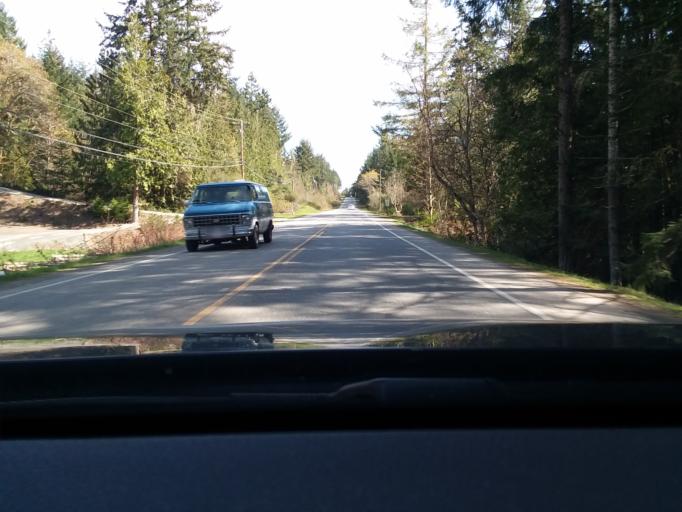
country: CA
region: British Columbia
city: North Cowichan
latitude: 48.8621
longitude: -123.4912
